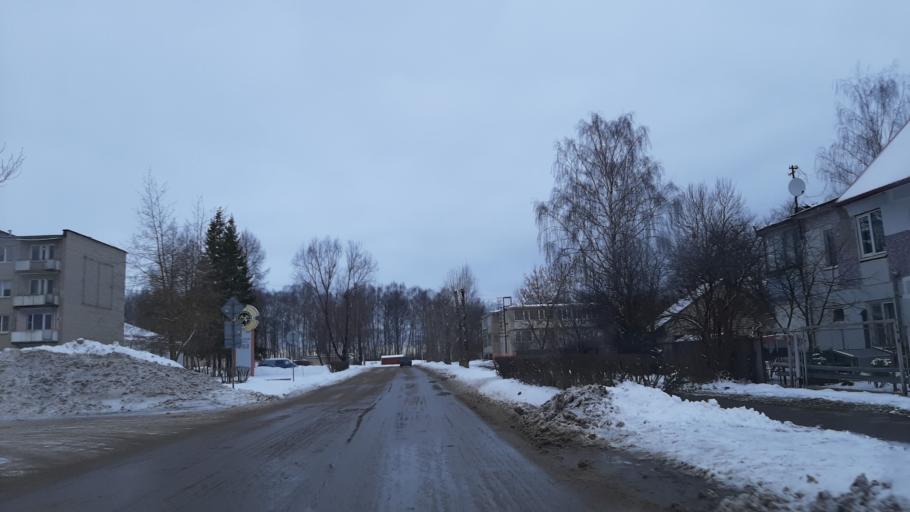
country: RU
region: Kostroma
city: Volgorechensk
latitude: 57.4436
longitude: 41.1469
